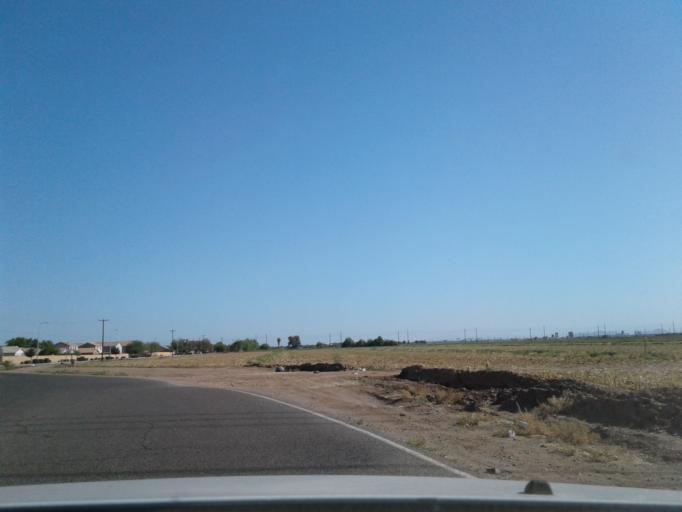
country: US
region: Arizona
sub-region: Maricopa County
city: Laveen
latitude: 33.4155
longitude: -112.1948
